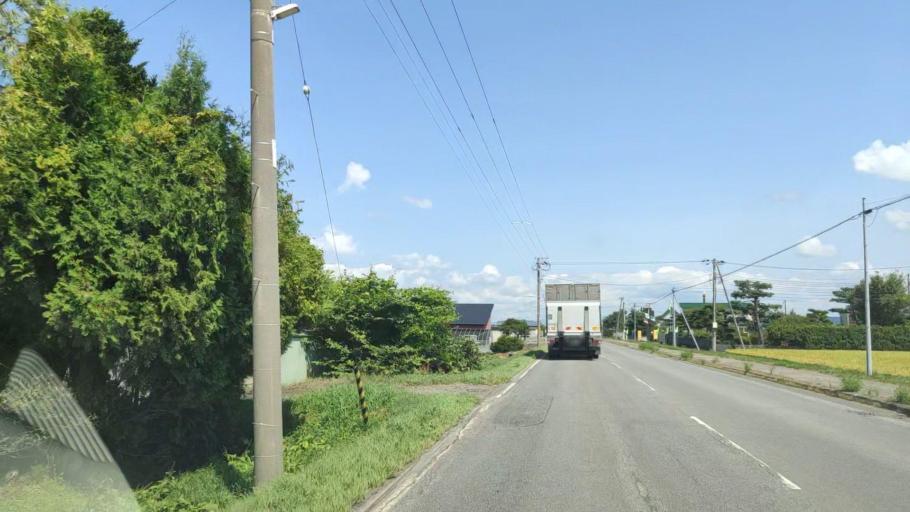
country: JP
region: Hokkaido
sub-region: Asahikawa-shi
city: Asahikawa
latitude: 43.7163
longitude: 142.4574
